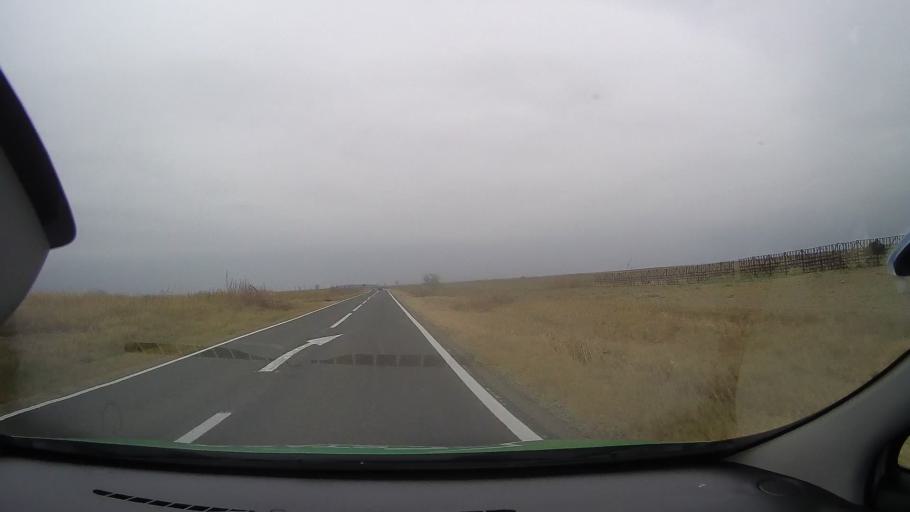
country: RO
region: Constanta
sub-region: Comuna Ciobanu
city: Ciobanu
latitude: 44.7025
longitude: 28.0242
